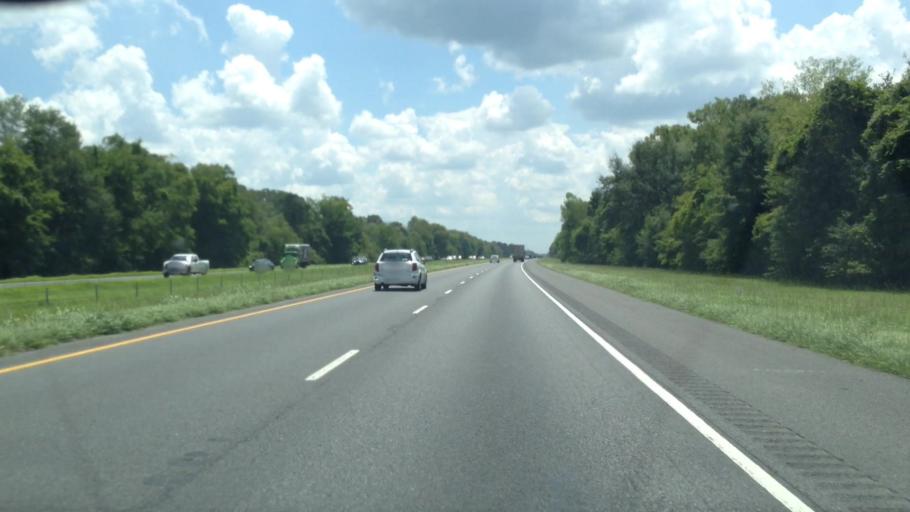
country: US
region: Louisiana
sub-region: Saint James Parish
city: Grand Point
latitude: 30.1482
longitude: -90.7752
